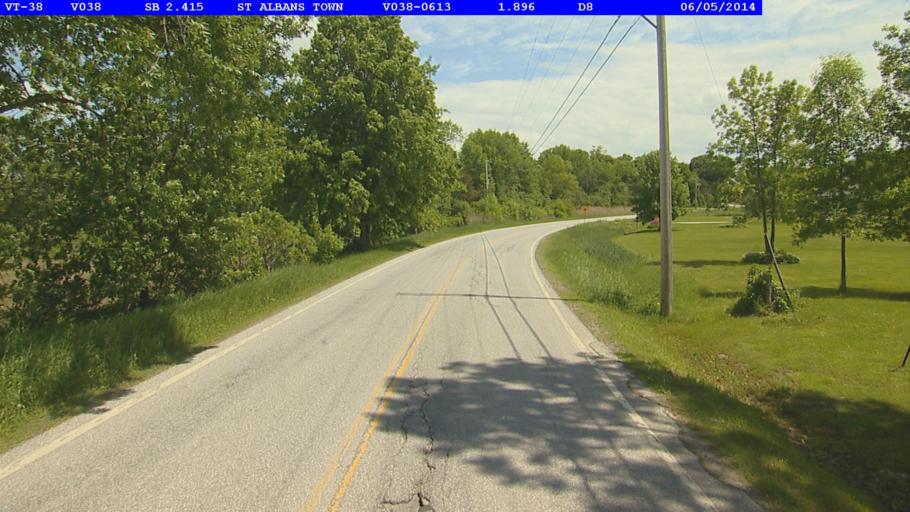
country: US
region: Vermont
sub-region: Franklin County
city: Saint Albans
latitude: 44.8460
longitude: -73.1109
